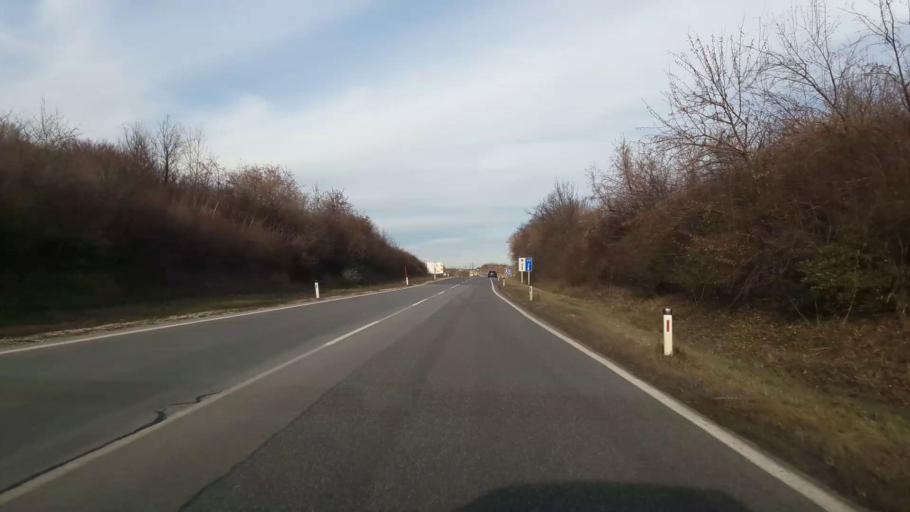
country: AT
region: Lower Austria
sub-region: Politischer Bezirk Mistelbach
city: Gaweinstal
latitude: 48.4912
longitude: 16.5966
